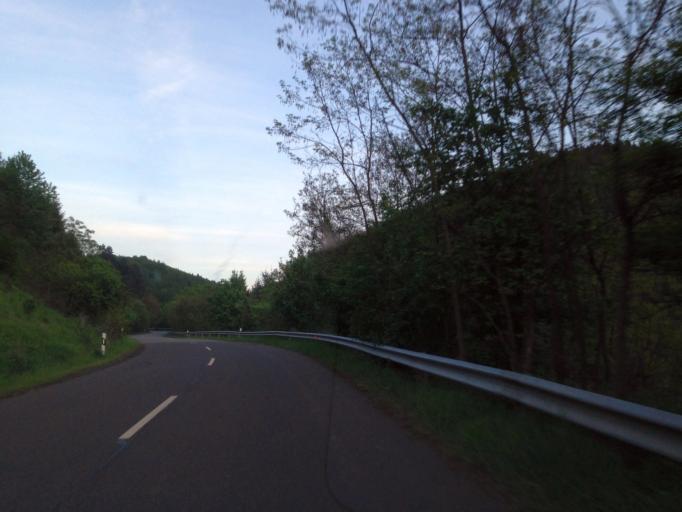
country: HU
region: Nograd
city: Batonyterenye
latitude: 47.8986
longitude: 19.8183
